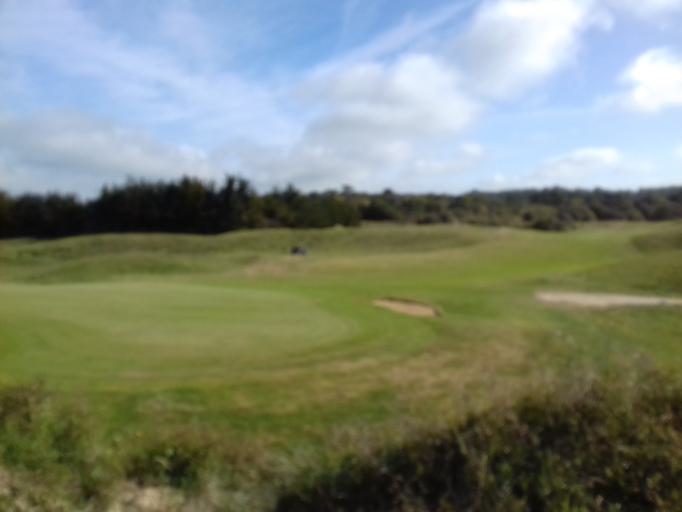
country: FR
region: Pays de la Loire
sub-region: Departement de la Vendee
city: Saint-Jean-de-Monts
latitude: 46.7966
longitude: -2.1016
